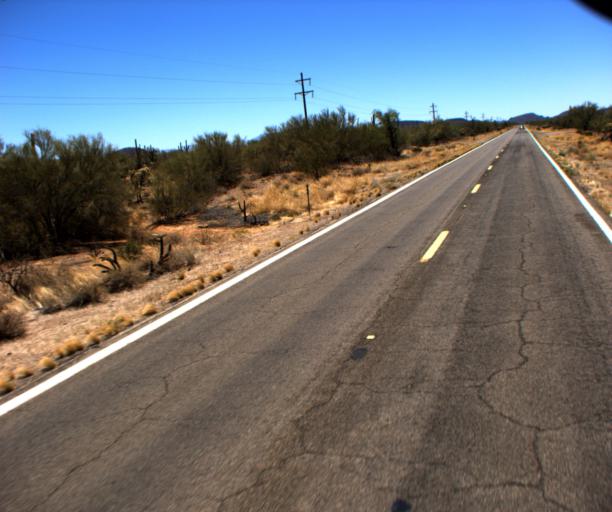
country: US
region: Arizona
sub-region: Pima County
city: Sells
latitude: 32.0205
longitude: -112.0017
